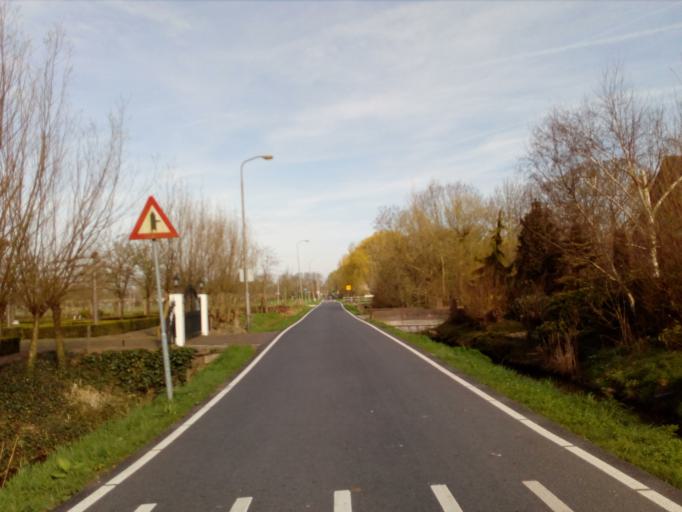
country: NL
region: South Holland
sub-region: Gemeente Delft
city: Delft
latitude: 51.9797
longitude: 4.3556
